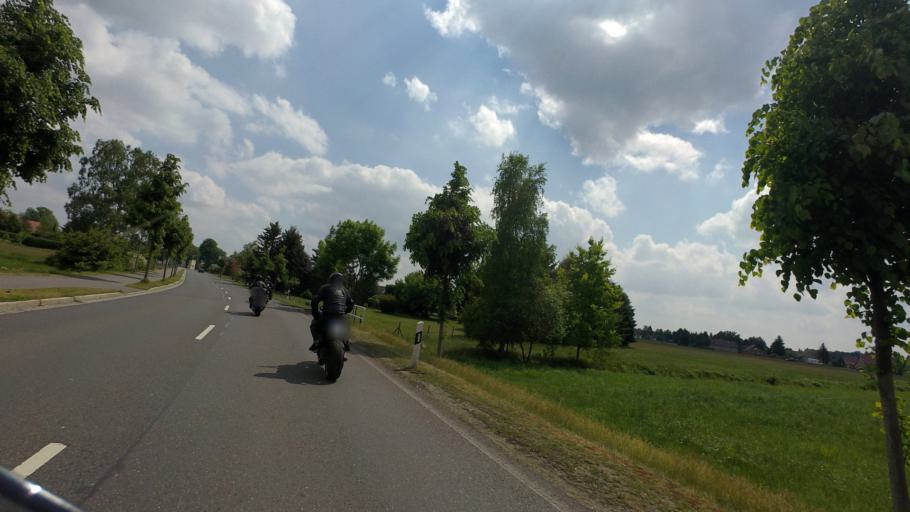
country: DE
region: Saxony
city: Weisskeissel
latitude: 51.4964
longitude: 14.7168
